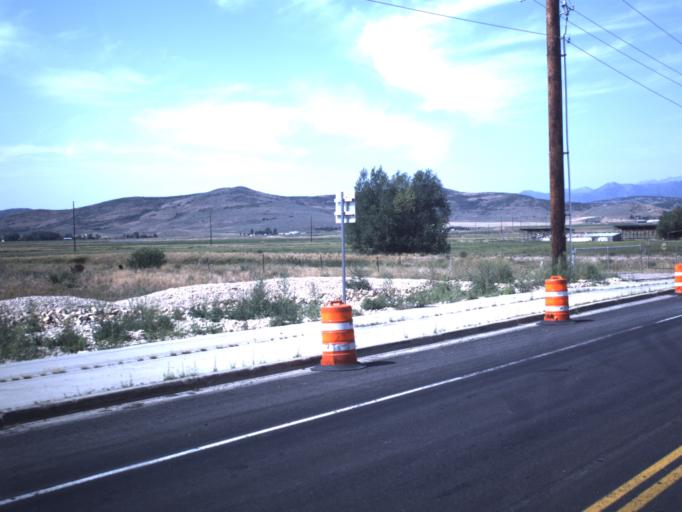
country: US
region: Utah
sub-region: Summit County
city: Kamas
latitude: 40.6399
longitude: -111.2856
